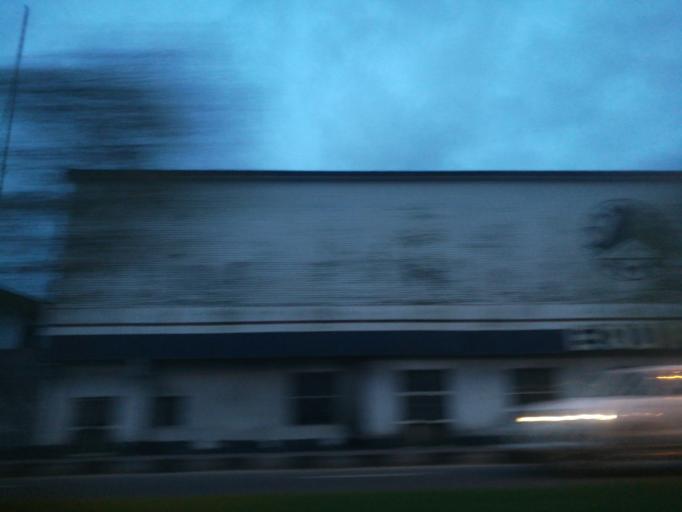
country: NG
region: Rivers
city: Port Harcourt
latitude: 4.7801
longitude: 7.0069
